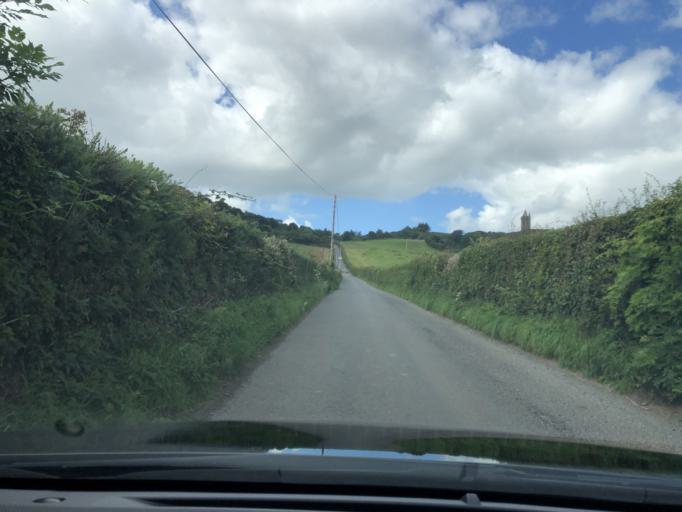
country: GB
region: Northern Ireland
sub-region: Ards District
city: Newtownards
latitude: 54.5731
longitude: -5.7157
